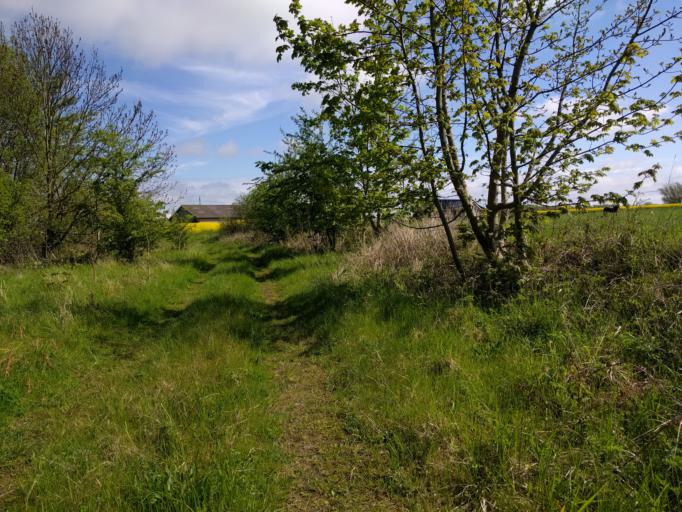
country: DK
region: South Denmark
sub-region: Kerteminde Kommune
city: Langeskov
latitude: 55.3873
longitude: 10.5624
